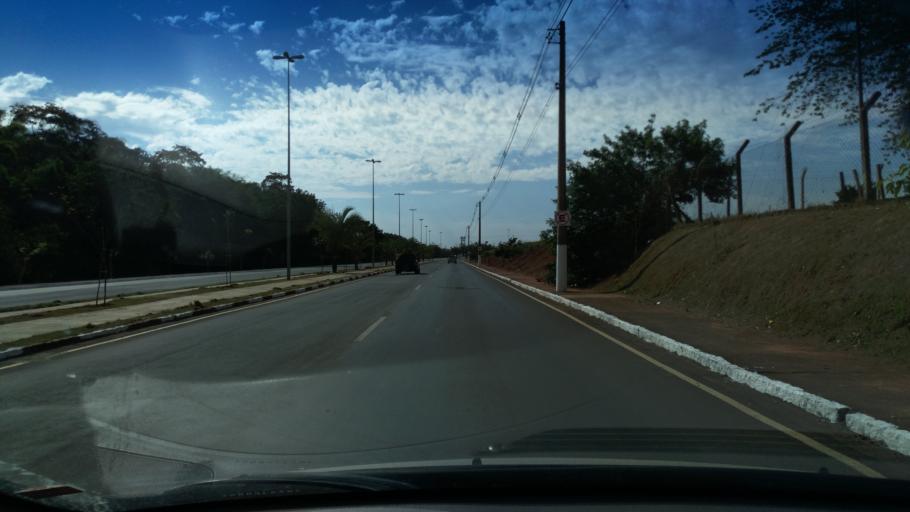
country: BR
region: Sao Paulo
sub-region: Jaguariuna
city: Jaguariuna
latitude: -22.6263
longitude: -47.0624
